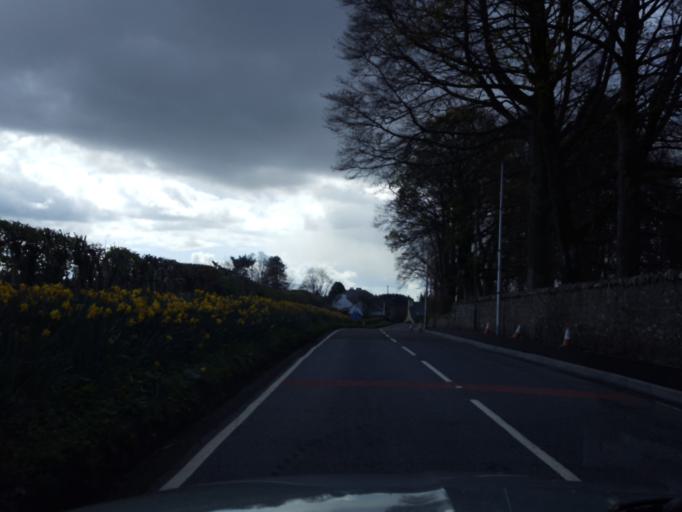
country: GB
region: Scotland
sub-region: Clackmannanshire
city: Dollar
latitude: 56.1919
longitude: -3.6082
